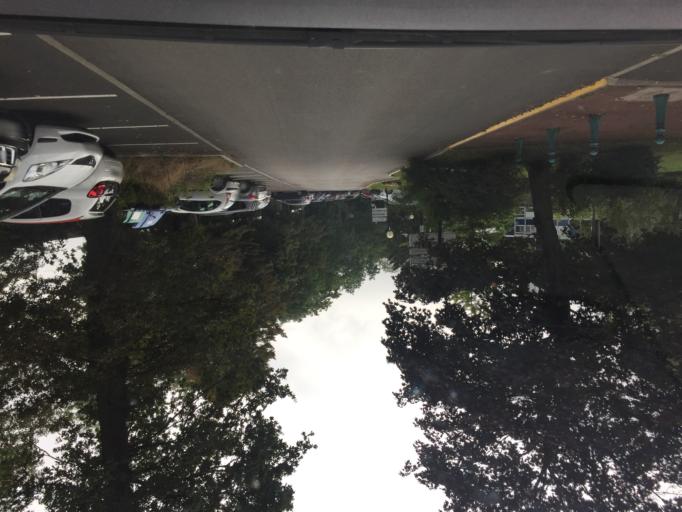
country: FR
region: Ile-de-France
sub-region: Departement des Yvelines
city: Jouy-en-Josas
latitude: 48.7561
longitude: 2.1625
